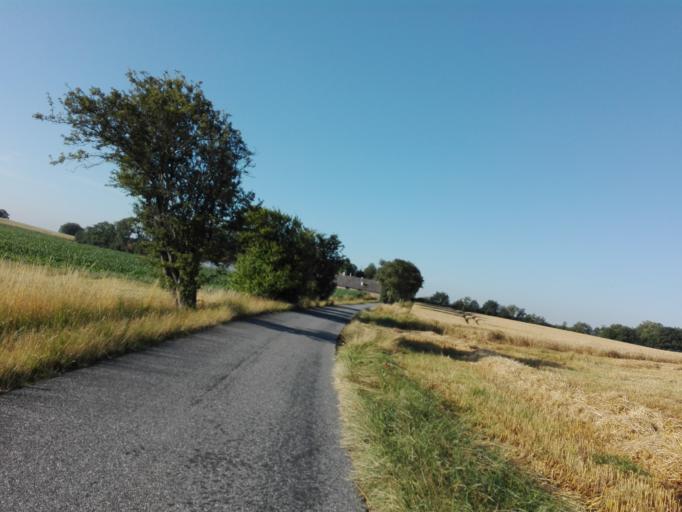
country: DK
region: Central Jutland
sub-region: Arhus Kommune
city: Tranbjerg
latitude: 56.0603
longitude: 10.1272
